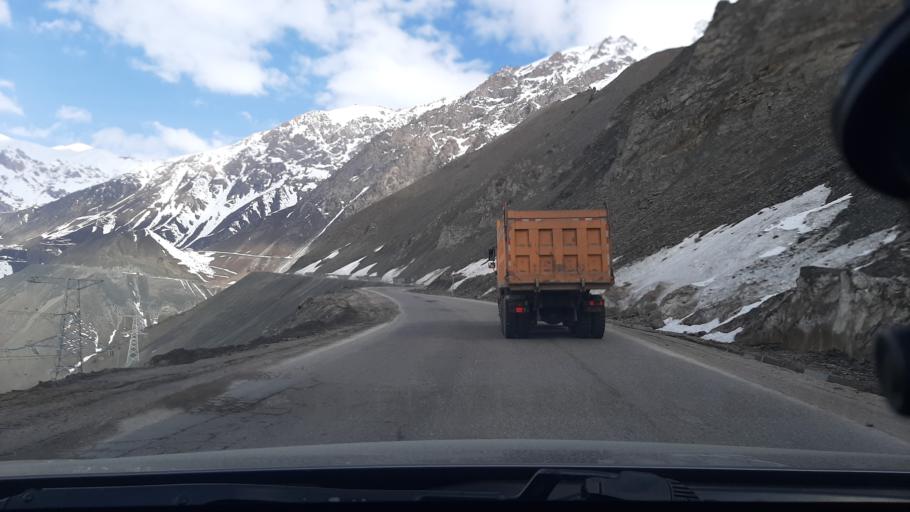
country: TJ
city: Tagob
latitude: 39.0501
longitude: 68.7405
